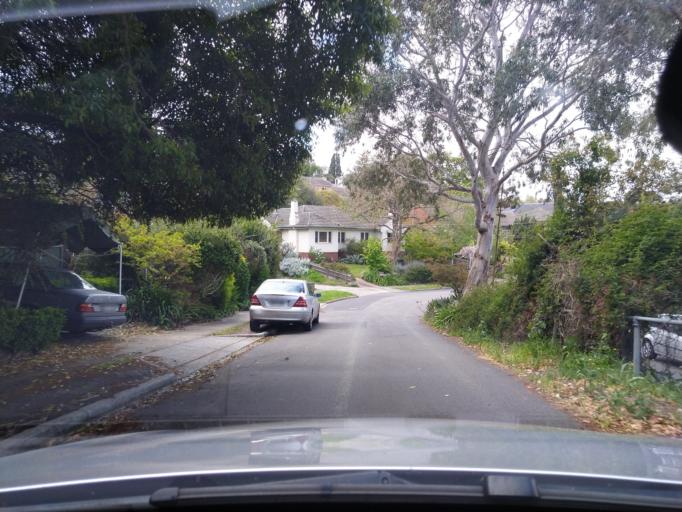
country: AU
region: Victoria
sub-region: Banyule
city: Bellfield
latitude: -37.7642
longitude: 145.0503
